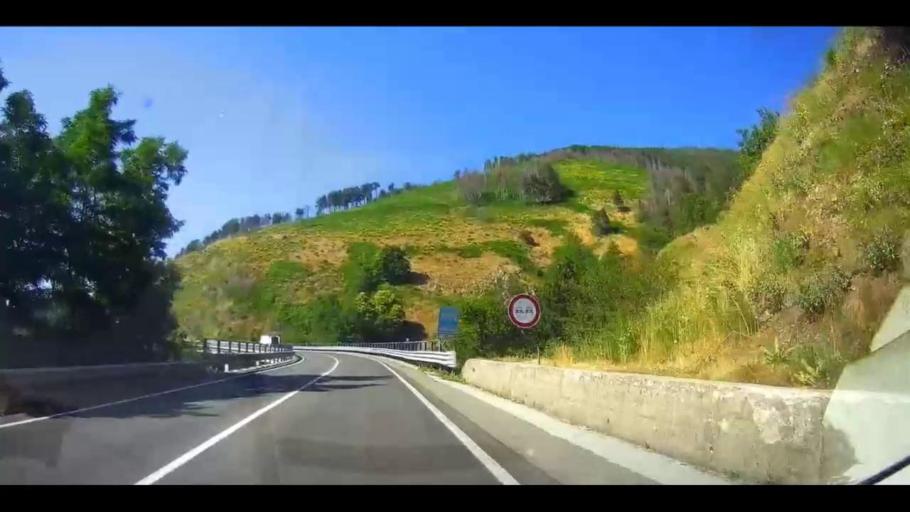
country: IT
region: Calabria
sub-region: Provincia di Cosenza
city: Celico
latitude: 39.3256
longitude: 16.3626
